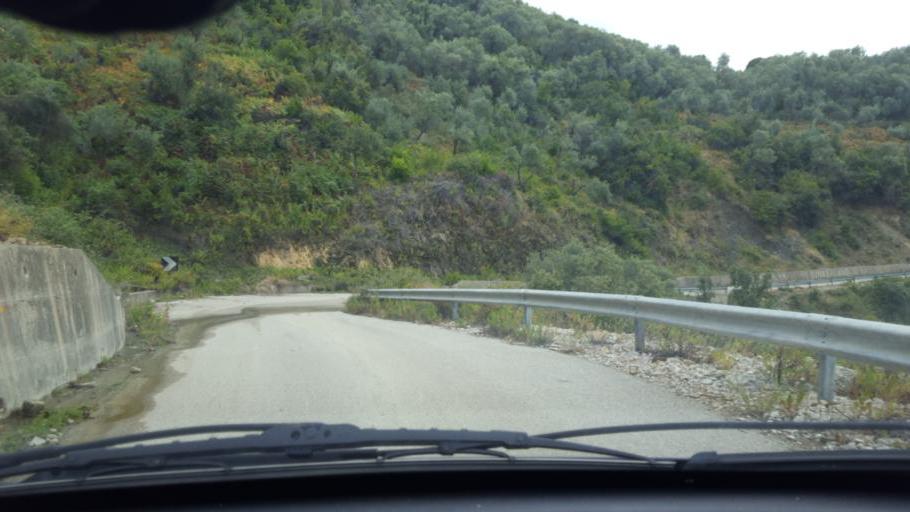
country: AL
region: Vlore
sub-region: Rrethi i Sarandes
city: Lukove
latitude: 39.9849
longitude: 19.9169
